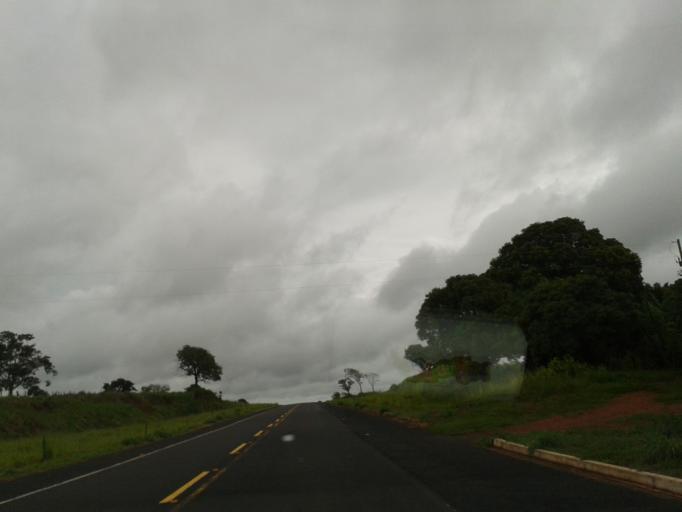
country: BR
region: Minas Gerais
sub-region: Santa Vitoria
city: Santa Vitoria
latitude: -19.2289
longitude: -50.0187
